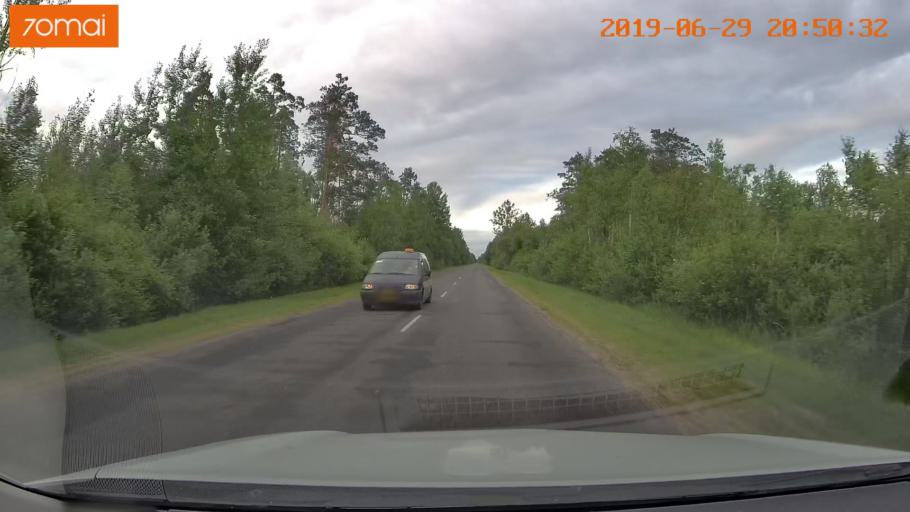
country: BY
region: Brest
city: Hantsavichy
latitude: 52.6777
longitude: 26.3373
